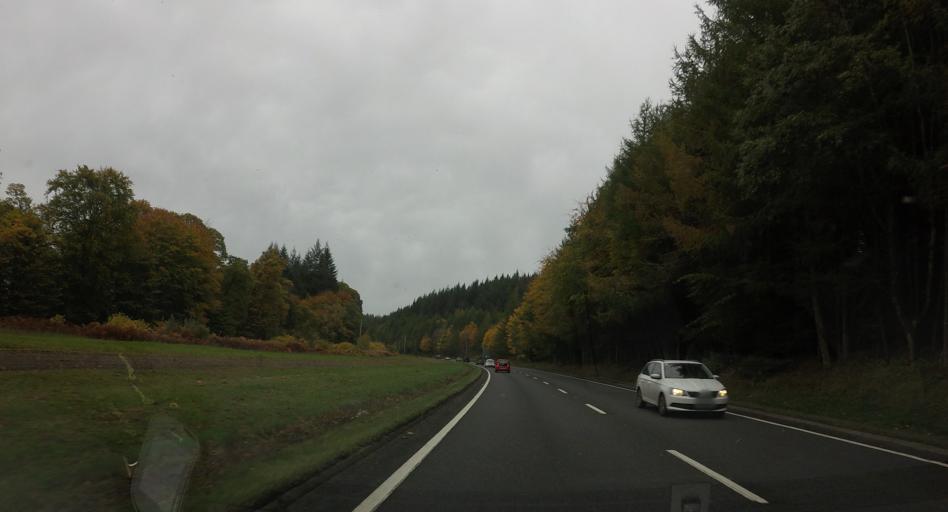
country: GB
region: Scotland
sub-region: Perth and Kinross
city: Bankfoot
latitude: 56.5685
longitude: -3.6235
